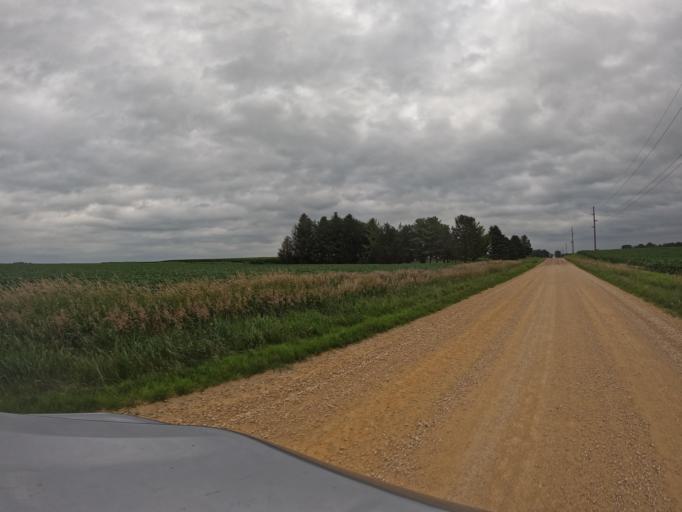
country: US
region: Iowa
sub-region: Clinton County
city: De Witt
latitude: 41.7863
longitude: -90.4590
